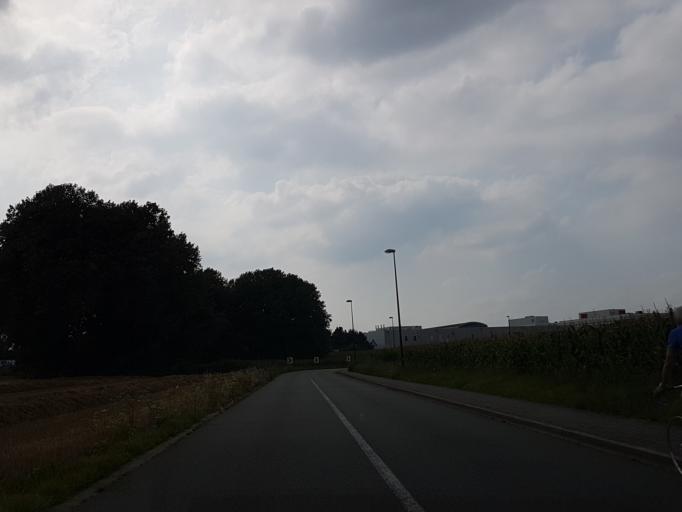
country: BE
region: Flanders
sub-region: Provincie Vlaams-Brabant
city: Diegem
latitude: 50.8793
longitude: 4.4436
